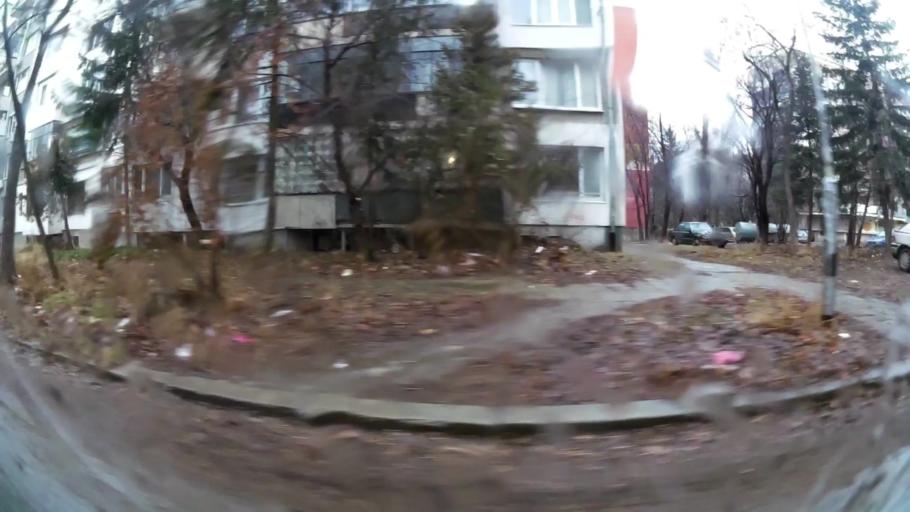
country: BG
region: Sofia-Capital
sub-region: Stolichna Obshtina
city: Sofia
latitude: 42.6510
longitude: 23.3710
